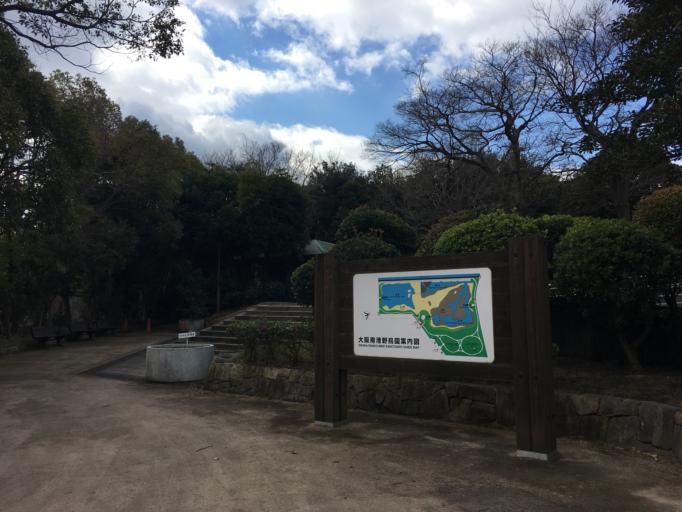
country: JP
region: Hyogo
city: Amagasaki
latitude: 34.6349
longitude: 135.4014
